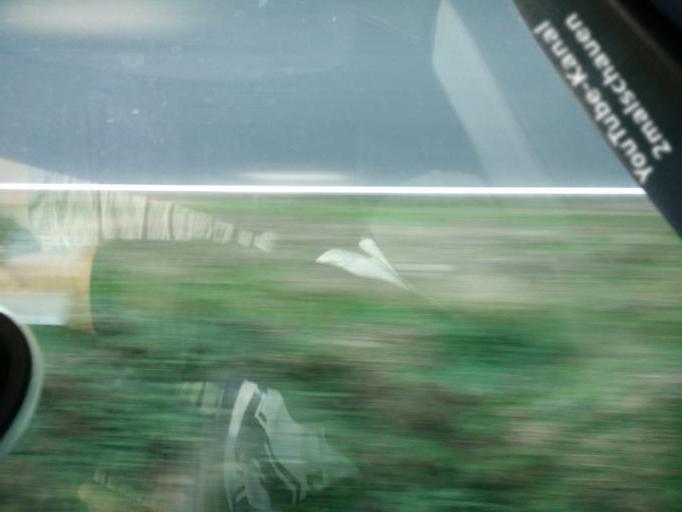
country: DE
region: Saxony
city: Kriebstein
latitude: 51.0583
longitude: 13.0215
